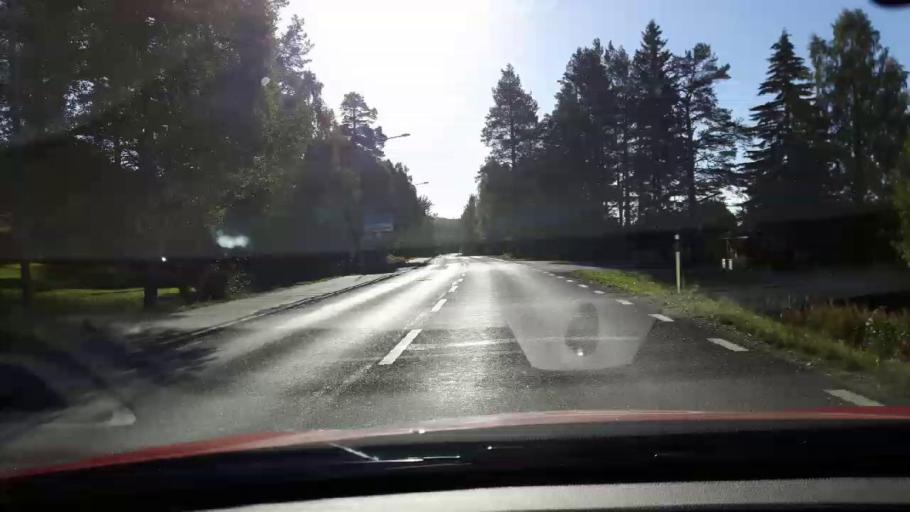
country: SE
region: Jaemtland
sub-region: OEstersunds Kommun
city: Brunflo
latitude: 62.9579
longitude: 15.0365
